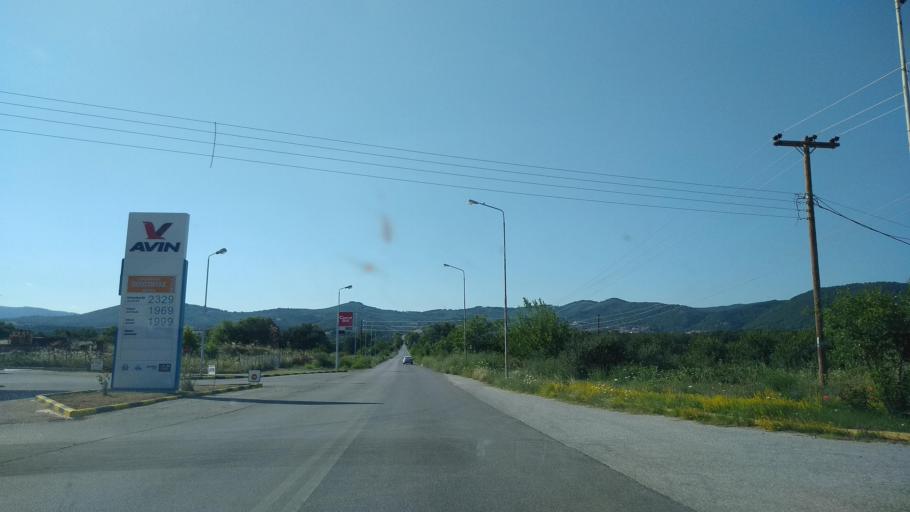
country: GR
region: Central Macedonia
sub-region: Nomos Chalkidikis
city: Megali Panagia
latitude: 40.4178
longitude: 23.6911
